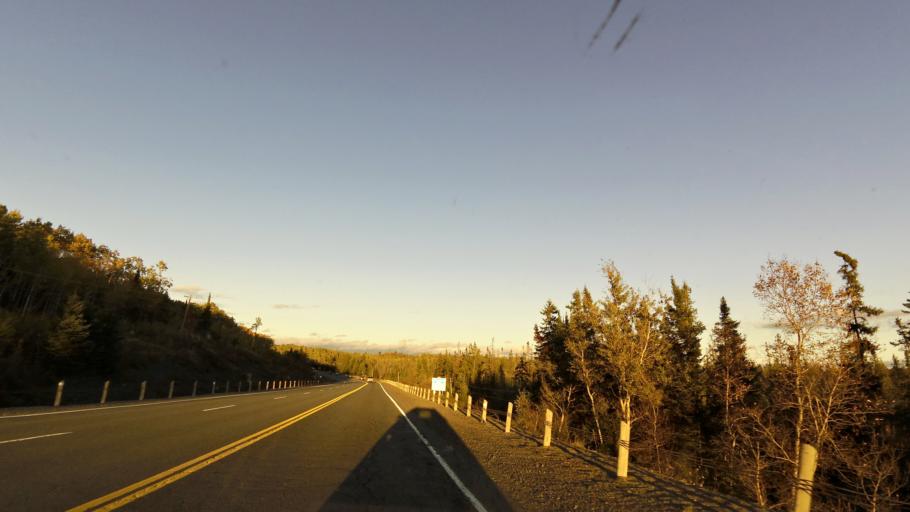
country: CA
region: Ontario
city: Espanola
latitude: 46.3508
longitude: -81.4451
